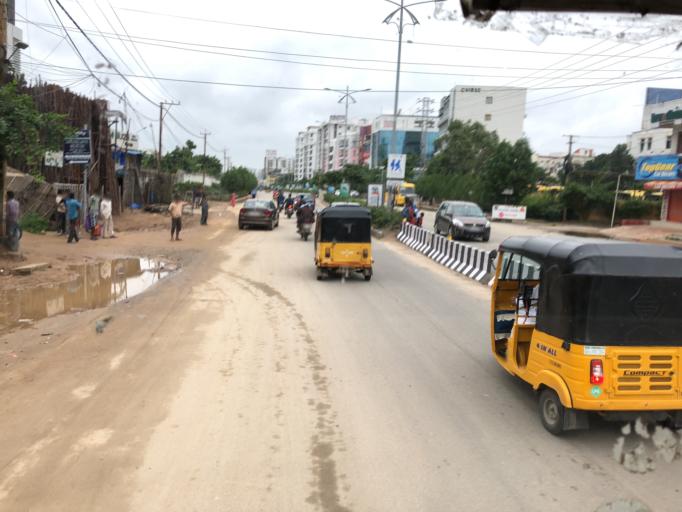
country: IN
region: Telangana
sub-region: Medak
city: Serilingampalle
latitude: 17.4615
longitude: 78.3522
